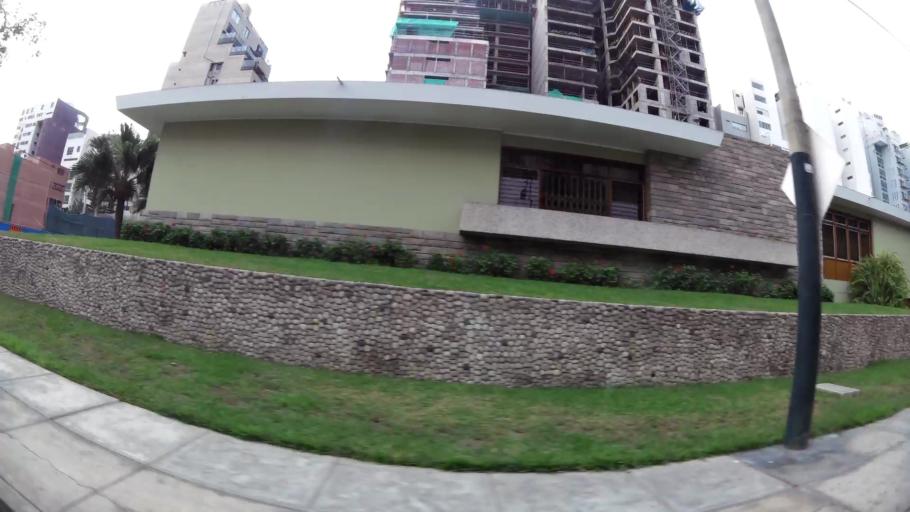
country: PE
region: Lima
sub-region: Lima
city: San Isidro
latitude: -12.1032
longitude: -77.0445
